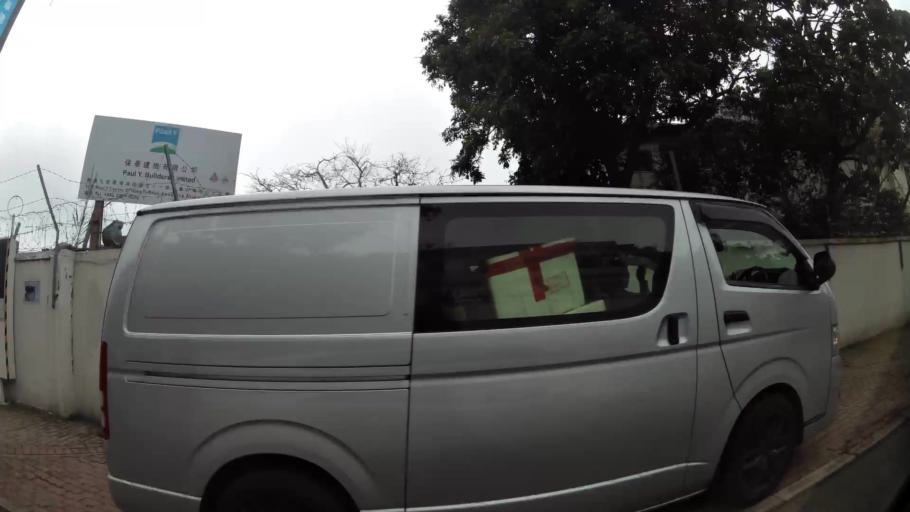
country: HK
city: Hong Kong
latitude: 22.2754
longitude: 114.1176
